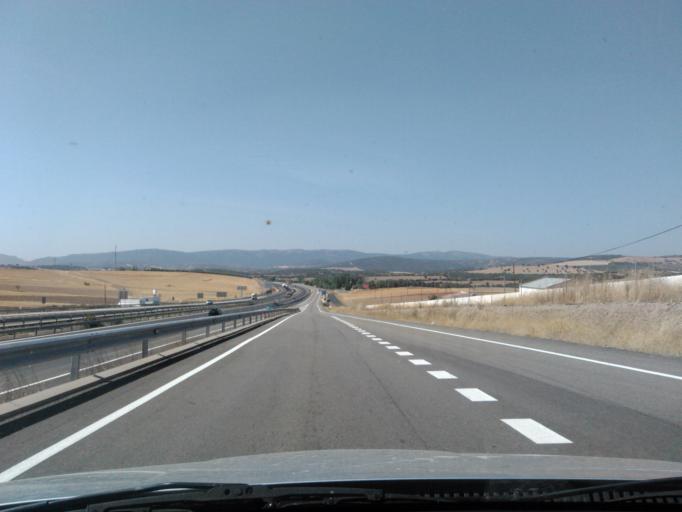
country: ES
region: Castille-La Mancha
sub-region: Provincia de Ciudad Real
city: Viso del Marques
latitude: 38.5051
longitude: -3.4996
